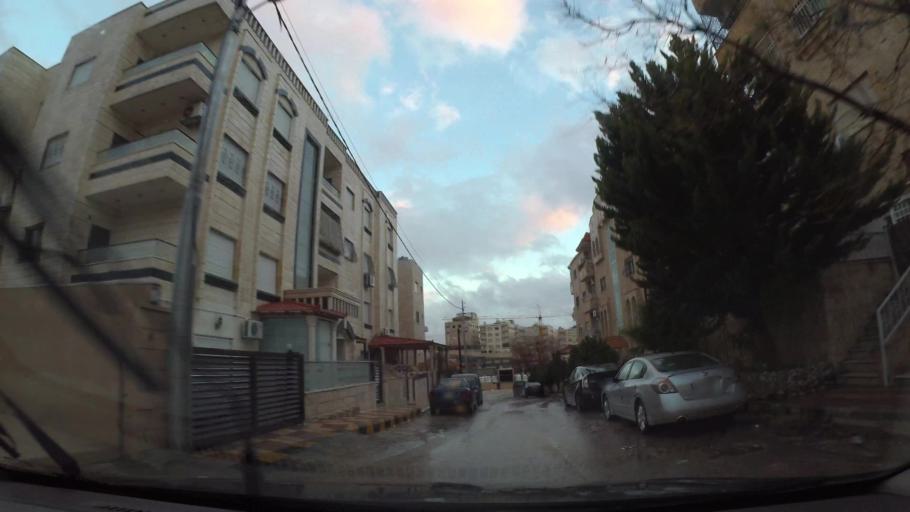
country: JO
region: Amman
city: Amman
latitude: 31.9951
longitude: 35.9214
